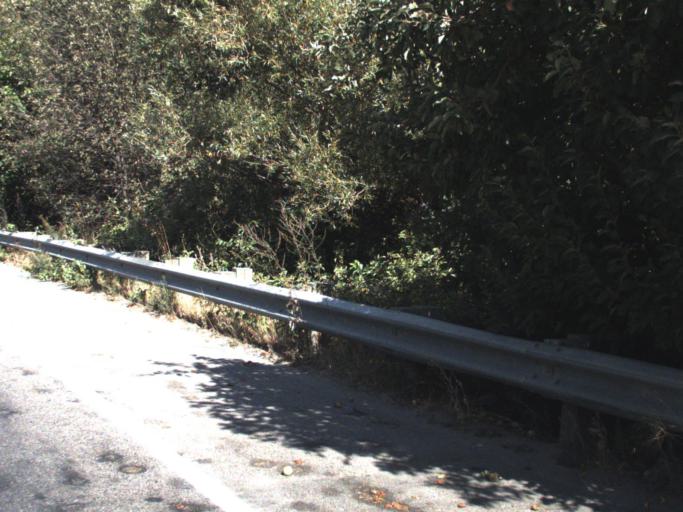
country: US
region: Washington
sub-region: Stevens County
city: Chewelah
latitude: 48.2839
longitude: -117.7159
